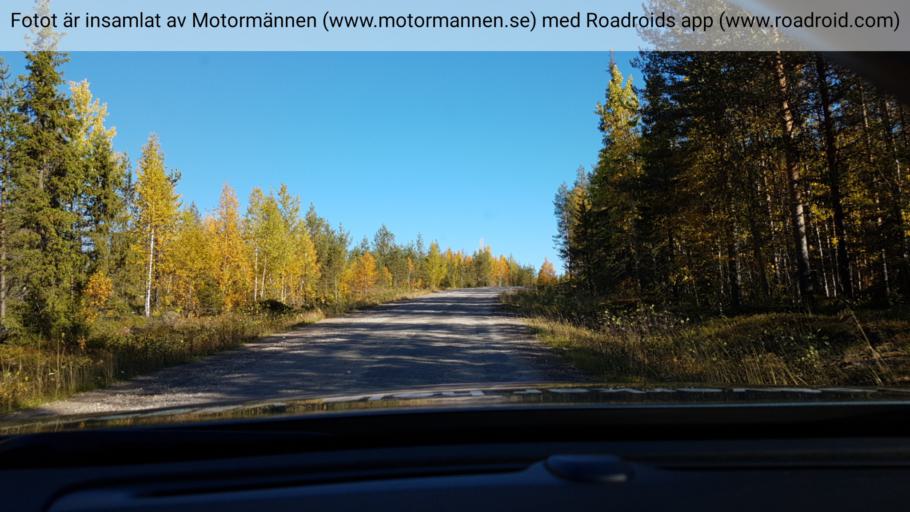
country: SE
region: Norrbotten
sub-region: Gallivare Kommun
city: Gaellivare
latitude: 66.5462
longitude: 20.9885
